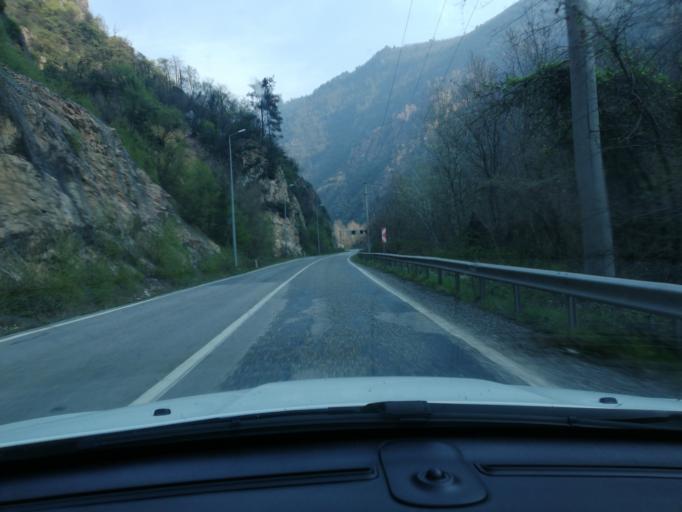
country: TR
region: Karabuk
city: Yenice
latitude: 41.1772
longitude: 32.4471
